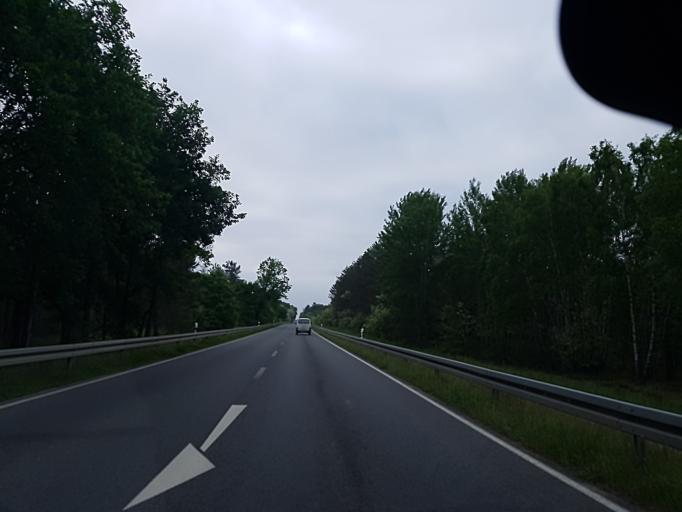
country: DE
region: Brandenburg
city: Schonewalde
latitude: 51.6357
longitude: 13.6240
